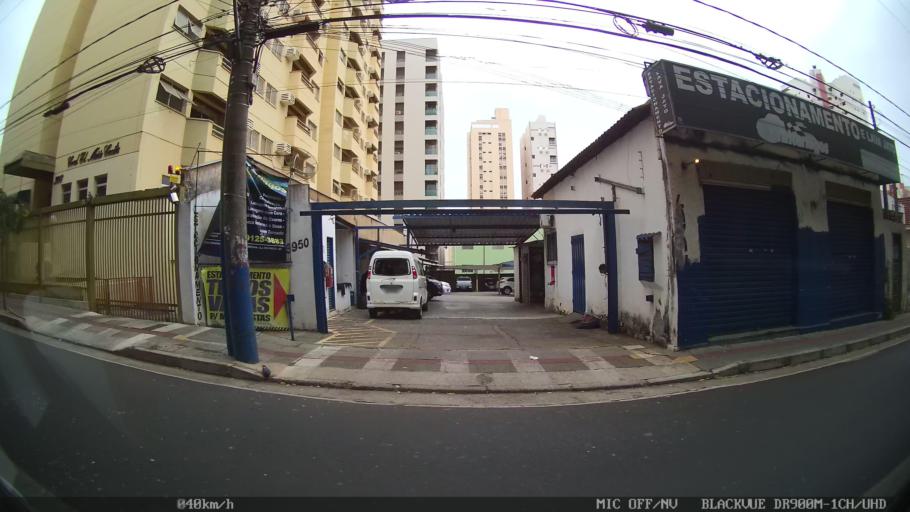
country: BR
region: Sao Paulo
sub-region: Sao Jose Do Rio Preto
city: Sao Jose do Rio Preto
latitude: -20.8164
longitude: -49.3875
